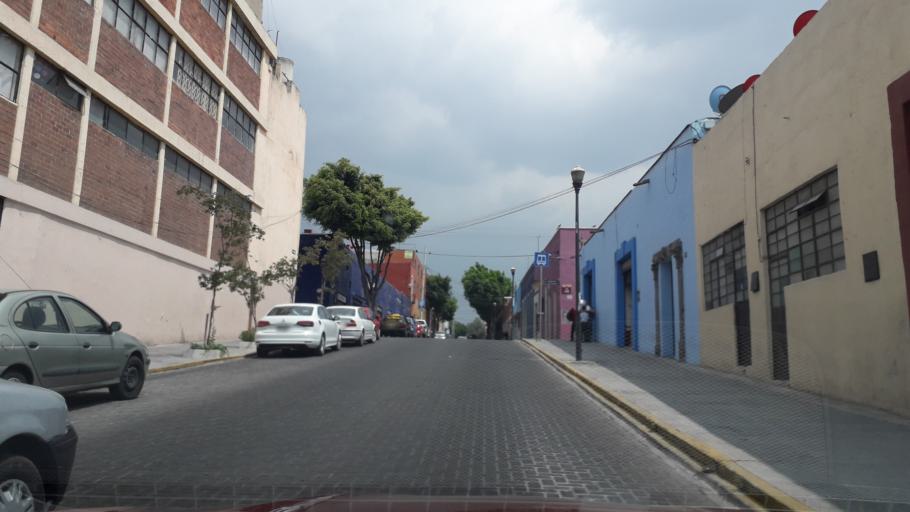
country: MX
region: Puebla
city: Puebla
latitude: 19.0409
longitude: -98.1918
